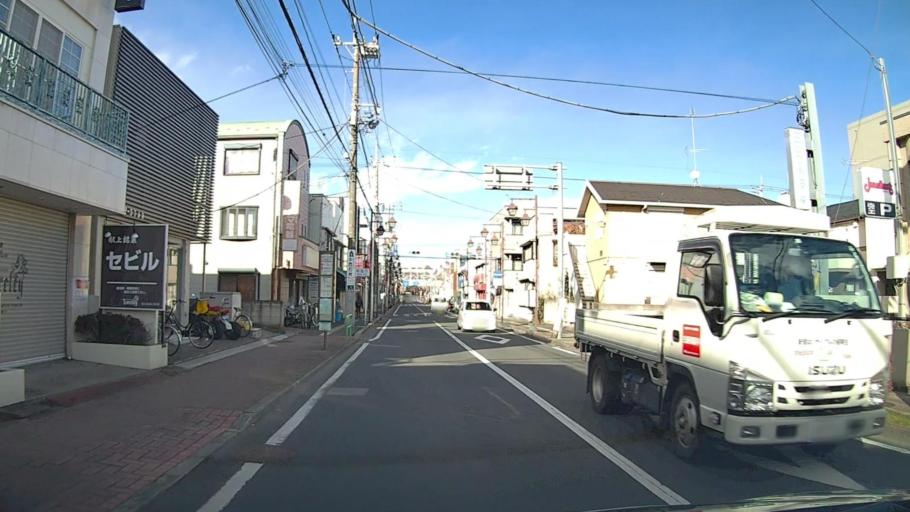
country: JP
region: Saitama
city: Asaka
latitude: 35.7747
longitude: 139.5860
